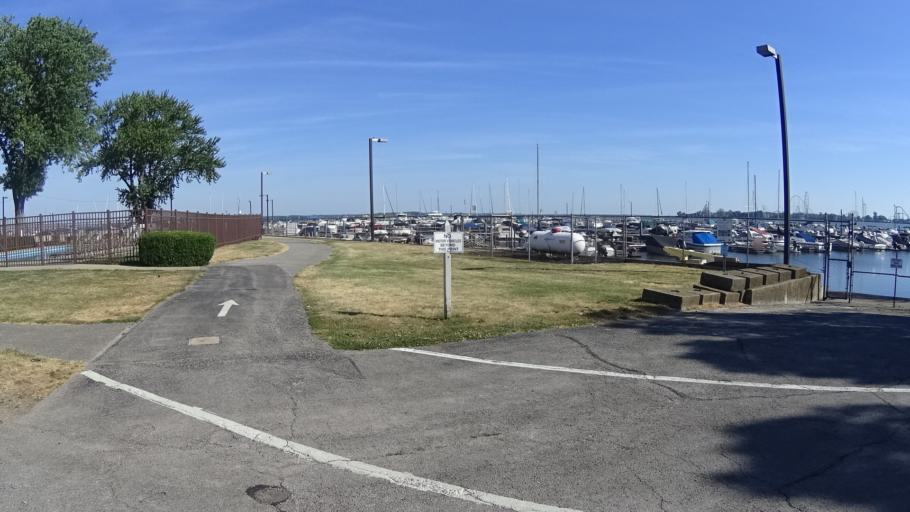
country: US
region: Ohio
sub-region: Erie County
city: Sandusky
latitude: 41.4615
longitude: -82.7005
